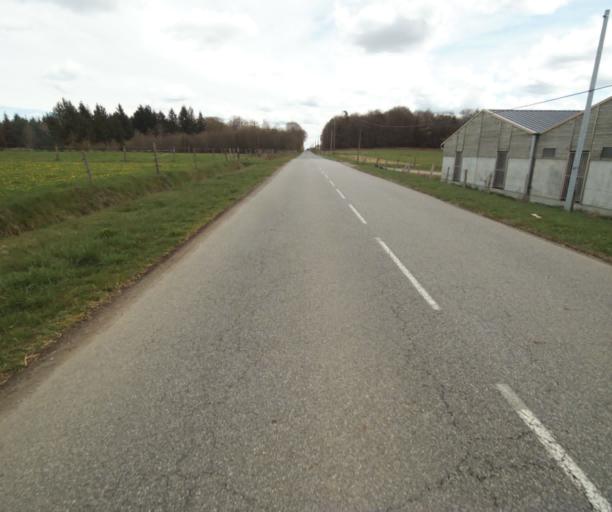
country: FR
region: Limousin
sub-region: Departement de la Correze
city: Laguenne
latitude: 45.2063
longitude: 1.8843
